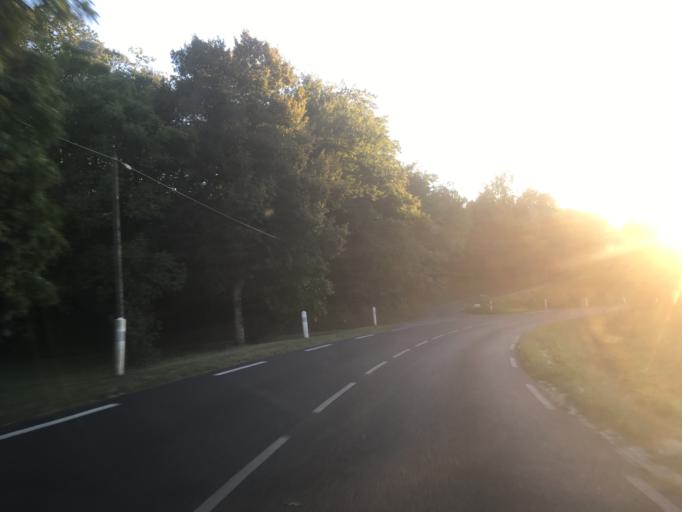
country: FR
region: Aquitaine
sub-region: Departement de la Dordogne
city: Sarlat-la-Caneda
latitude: 44.8497
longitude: 1.1897
